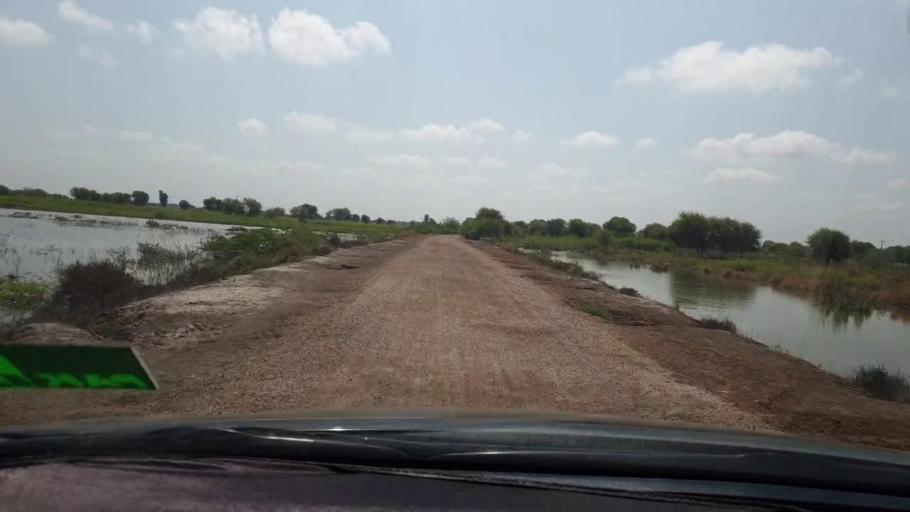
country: PK
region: Sindh
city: Tando Bago
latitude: 24.9388
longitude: 69.0930
